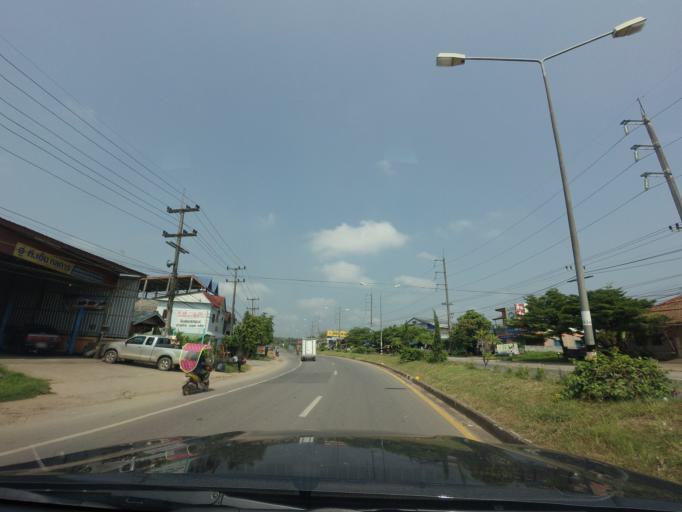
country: TH
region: Nan
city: Nan
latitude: 18.7836
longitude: 100.7466
